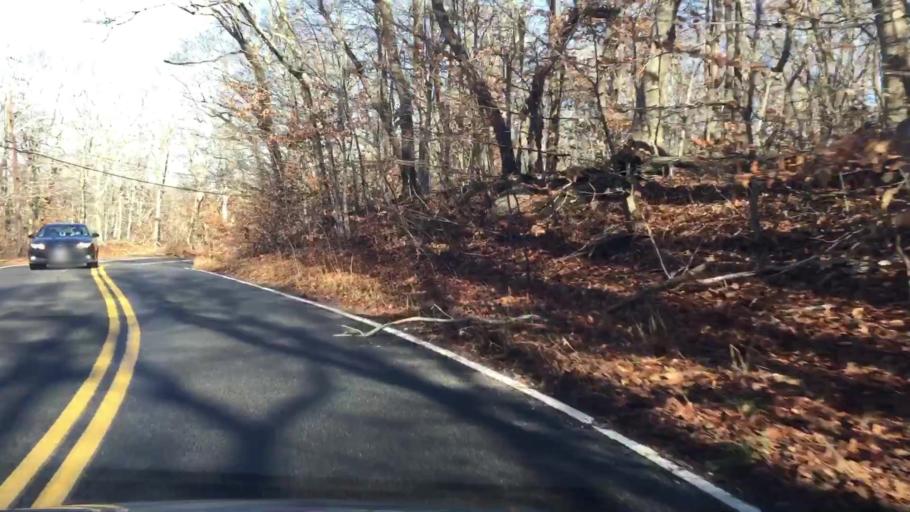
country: US
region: Massachusetts
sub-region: Barnstable County
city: Falmouth
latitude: 41.5339
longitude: -70.6592
